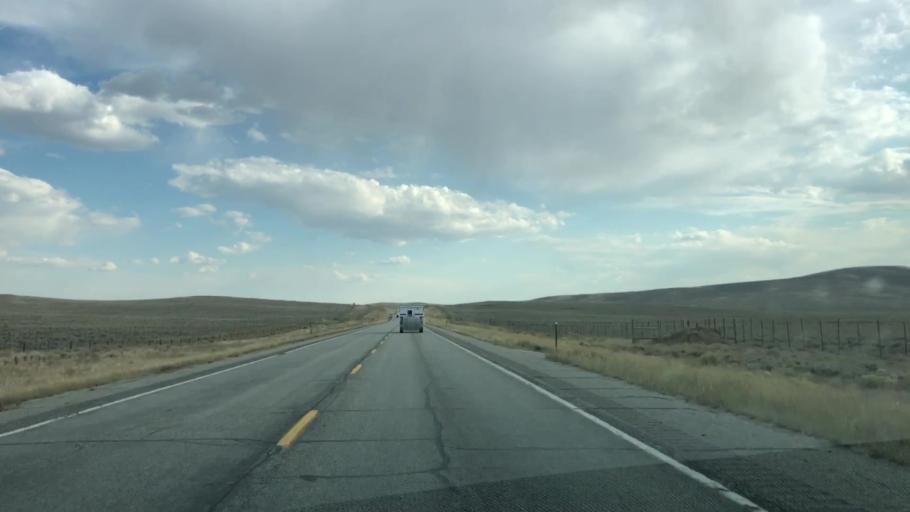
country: US
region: Wyoming
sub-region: Sublette County
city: Pinedale
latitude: 42.9300
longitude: -110.0811
